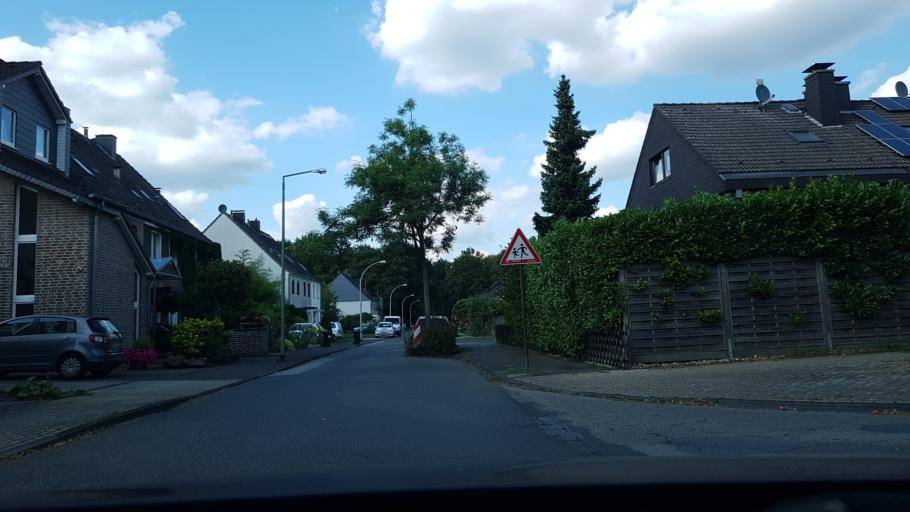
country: DE
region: North Rhine-Westphalia
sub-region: Regierungsbezirk Dusseldorf
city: Hochfeld
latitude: 51.3891
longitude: 6.7617
